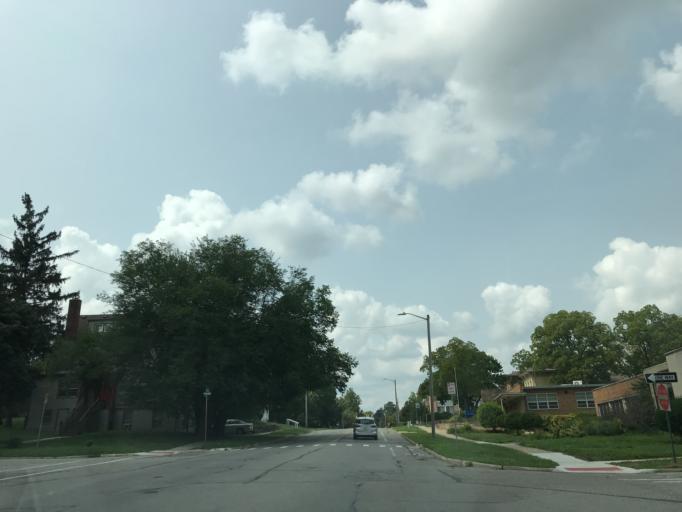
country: US
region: Michigan
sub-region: Washtenaw County
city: Ypsilanti
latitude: 42.2489
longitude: -83.6159
